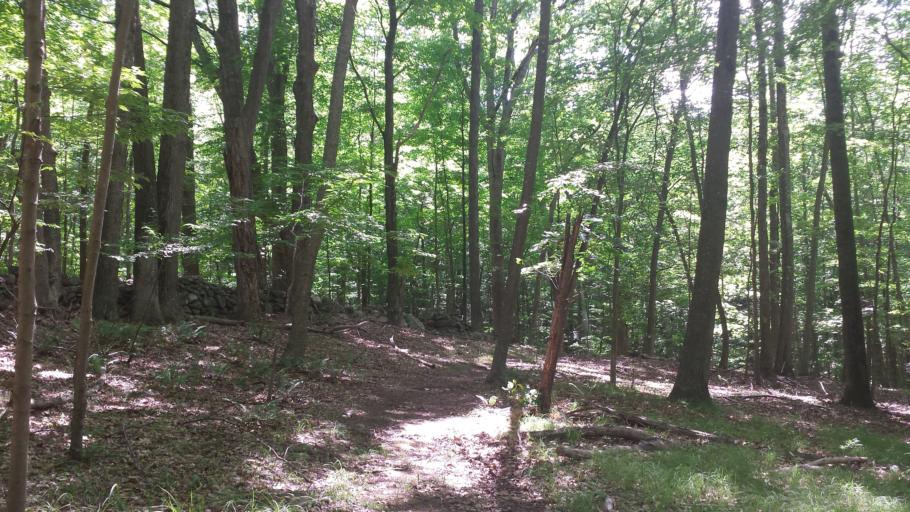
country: US
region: New York
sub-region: Westchester County
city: Pound Ridge
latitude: 41.2589
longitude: -73.5817
